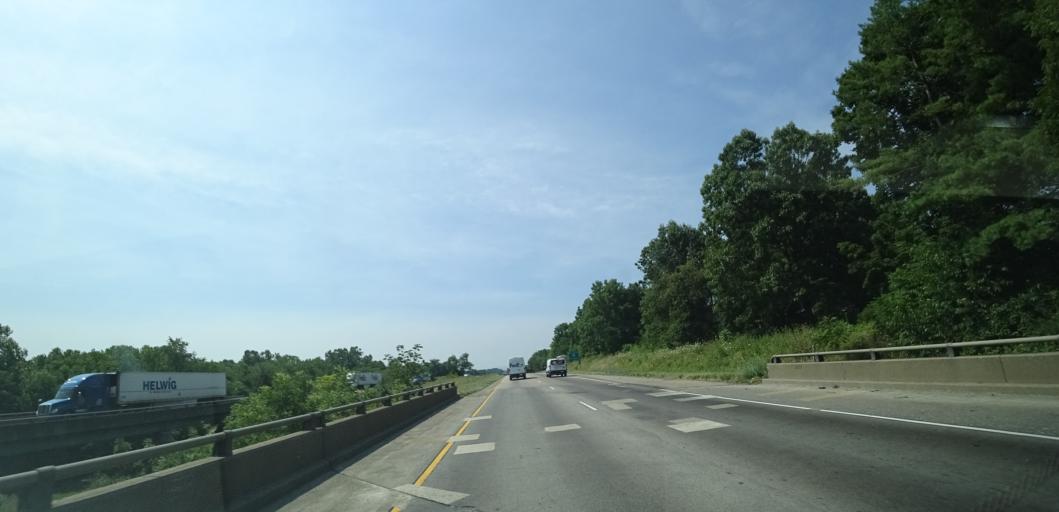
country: US
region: Virginia
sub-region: Augusta County
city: Verona
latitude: 38.2000
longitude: -78.9951
